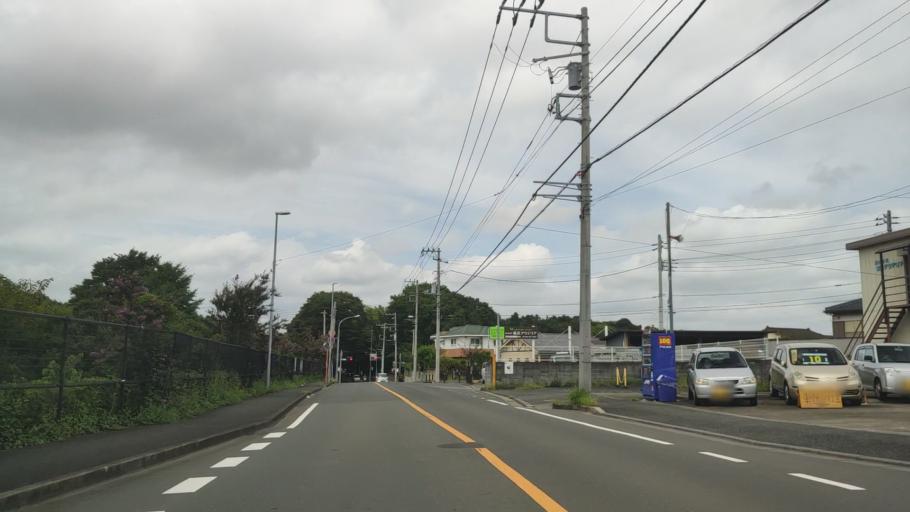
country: JP
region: Kanagawa
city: Minami-rinkan
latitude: 35.4824
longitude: 139.4751
